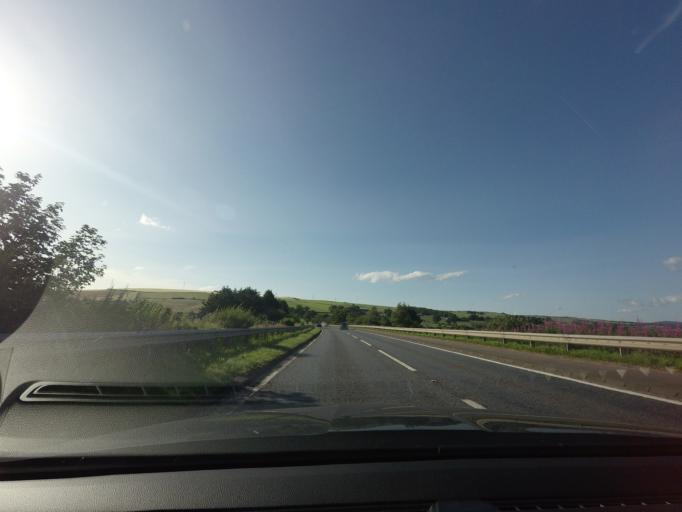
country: GB
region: Scotland
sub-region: Highland
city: Conon Bridge
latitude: 57.5770
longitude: -4.4337
